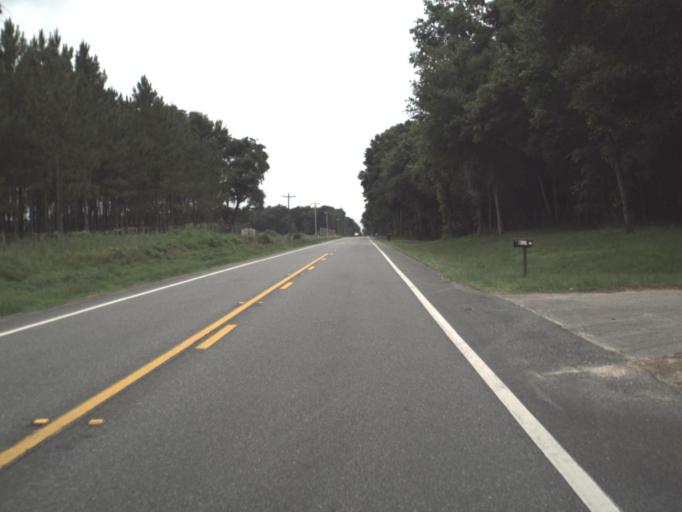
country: US
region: Florida
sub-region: Alachua County
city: Archer
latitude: 29.5547
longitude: -82.5305
